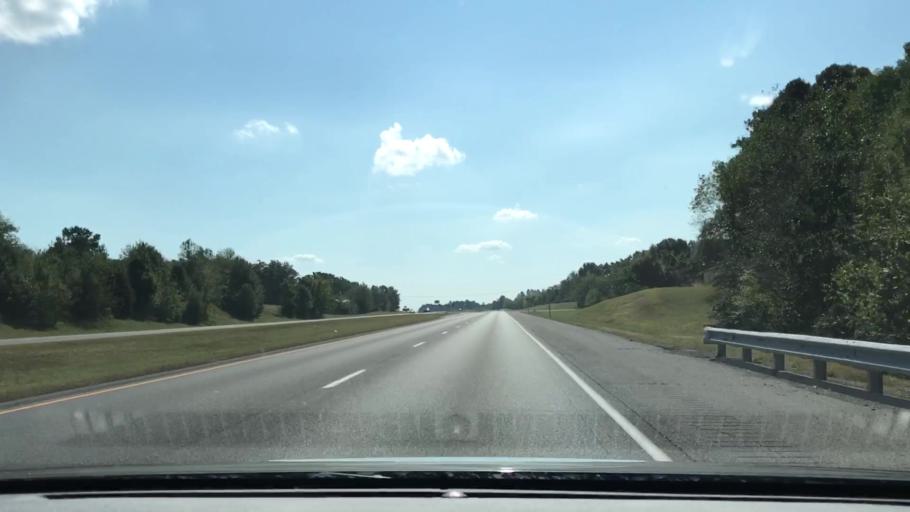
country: US
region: Kentucky
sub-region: Marshall County
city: Benton
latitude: 36.8018
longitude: -88.3417
